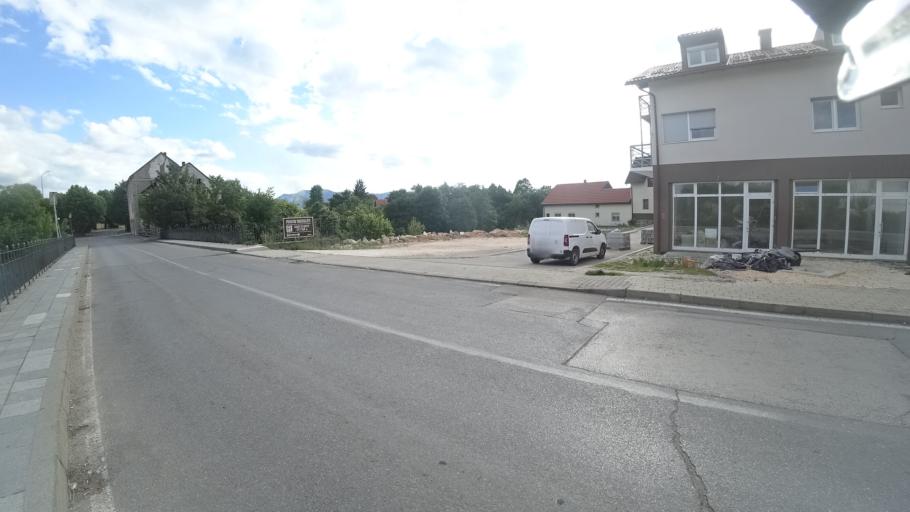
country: HR
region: Licko-Senjska
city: Gospic
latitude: 44.5447
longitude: 15.3778
